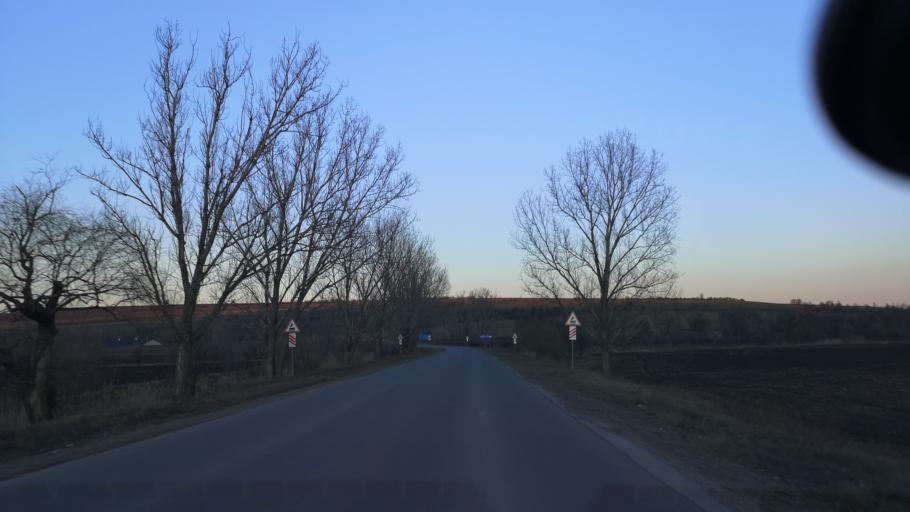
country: MD
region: Anenii Noi
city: Anenii Noi
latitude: 46.8890
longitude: 29.2393
